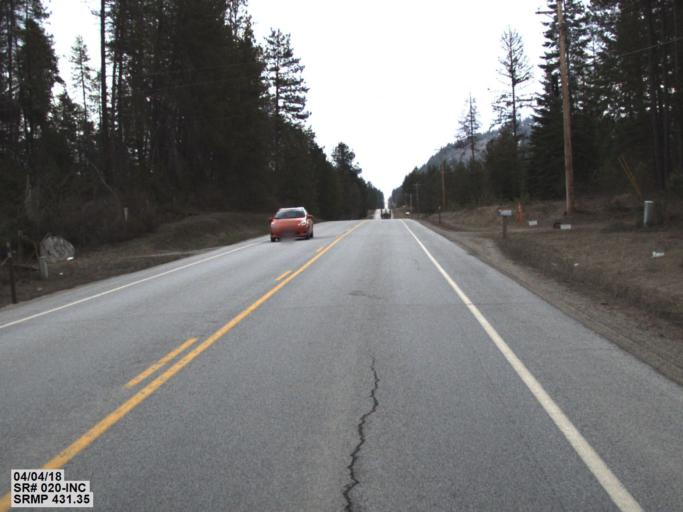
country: US
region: Washington
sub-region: Pend Oreille County
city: Newport
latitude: 48.2257
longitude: -117.1336
